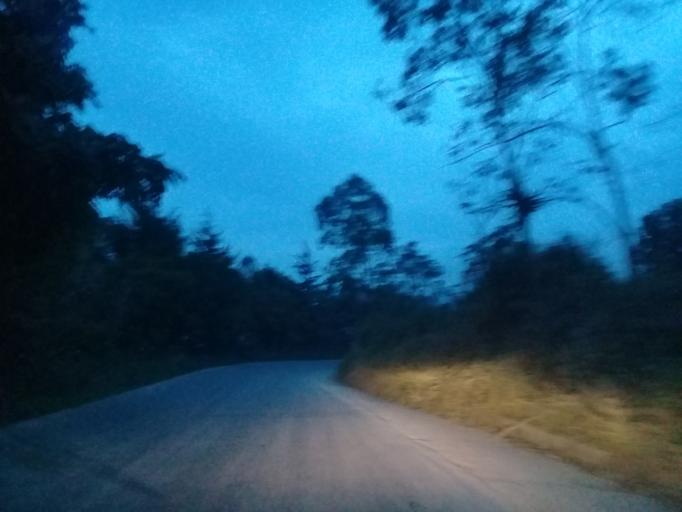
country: CO
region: Cundinamarca
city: Pacho
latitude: 5.1333
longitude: -74.1456
